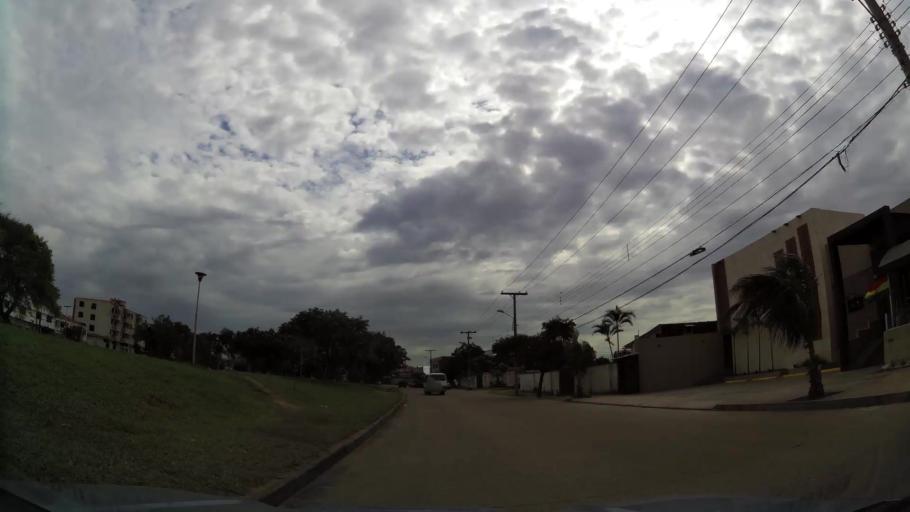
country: BO
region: Santa Cruz
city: Santa Cruz de la Sierra
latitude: -17.7549
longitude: -63.1902
